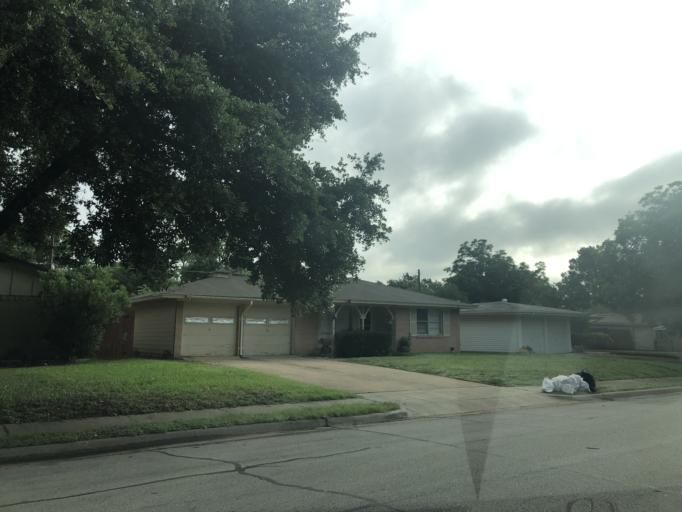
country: US
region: Texas
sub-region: Dallas County
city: Irving
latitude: 32.8049
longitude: -96.9789
